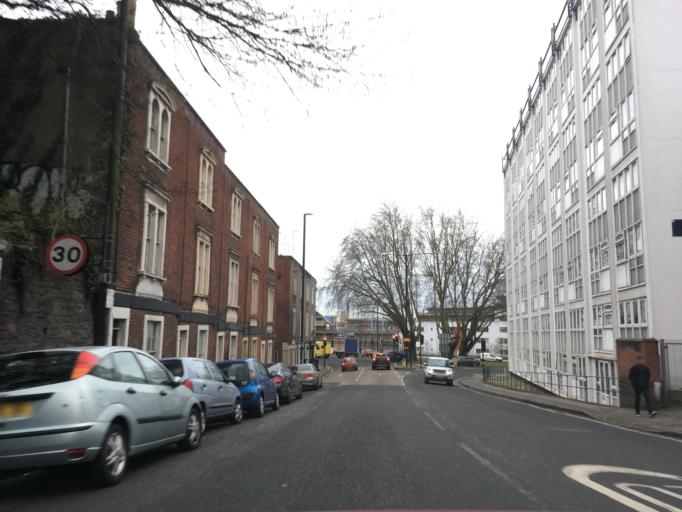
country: GB
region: England
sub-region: Bristol
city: Bristol
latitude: 51.4517
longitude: -2.6082
